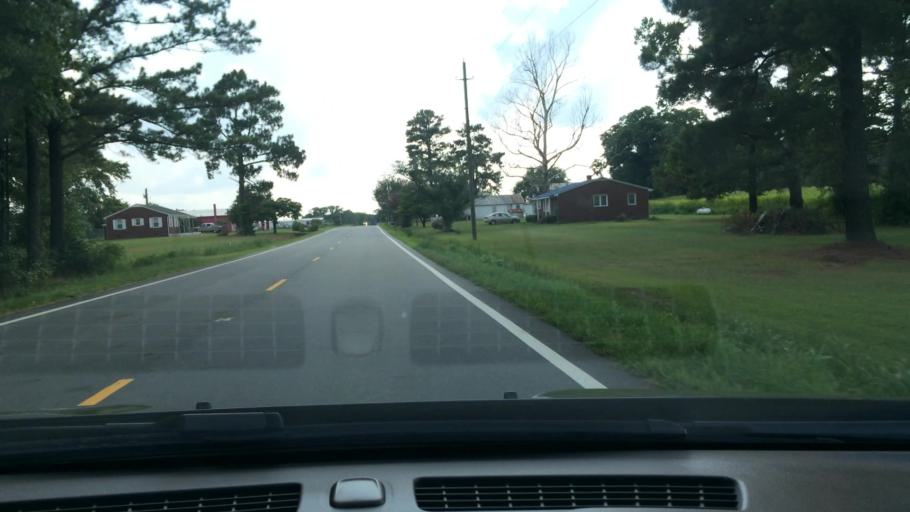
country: US
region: North Carolina
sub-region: Craven County
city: Vanceboro
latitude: 35.4223
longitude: -77.2268
